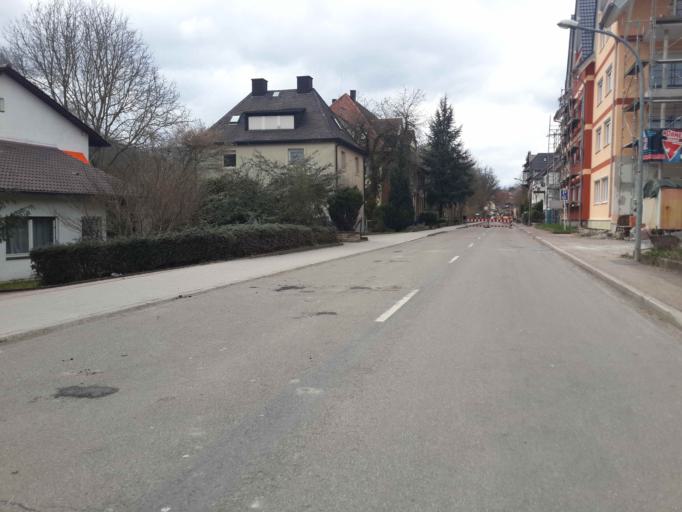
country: DE
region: Baden-Wuerttemberg
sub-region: Karlsruhe Region
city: Adelsheim
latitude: 49.3977
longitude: 9.3937
